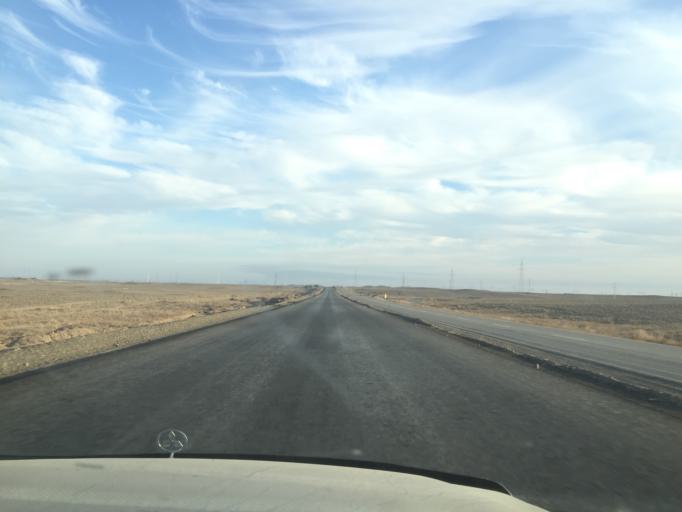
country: KZ
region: Almaty Oblysy
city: Ulken
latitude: 45.2197
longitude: 73.8619
